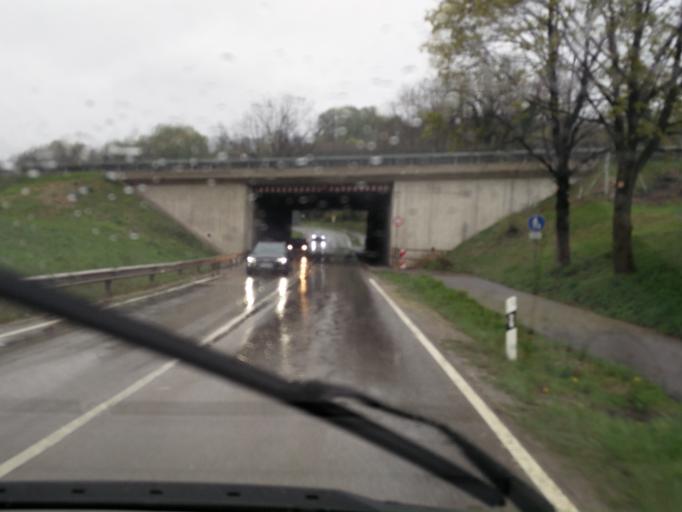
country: DE
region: Bavaria
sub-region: Upper Bavaria
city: Bernau am Chiemsee
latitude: 47.8159
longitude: 12.3628
